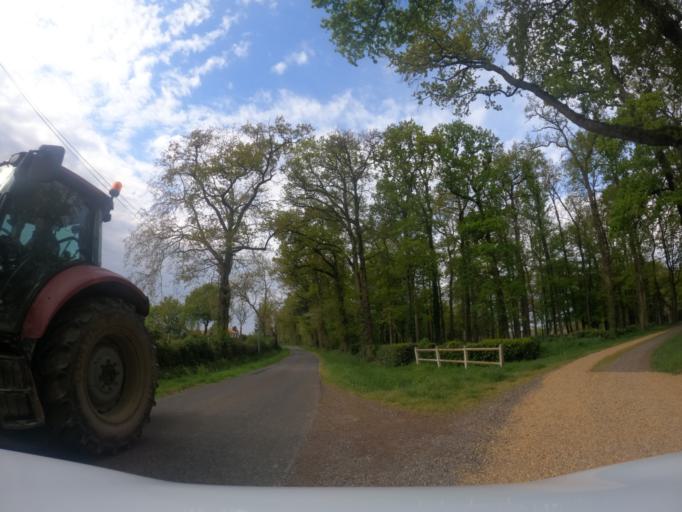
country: FR
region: Pays de la Loire
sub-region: Departement de la Vendee
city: Saint-Vincent-sur-Graon
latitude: 46.5405
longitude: -1.3849
